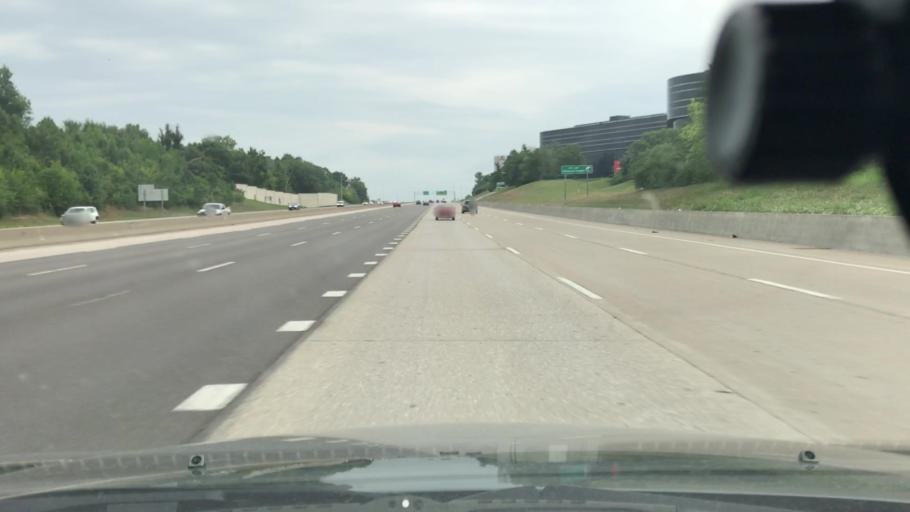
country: US
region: Missouri
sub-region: Saint Louis County
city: Maryland Heights
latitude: 38.6876
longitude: -90.4499
